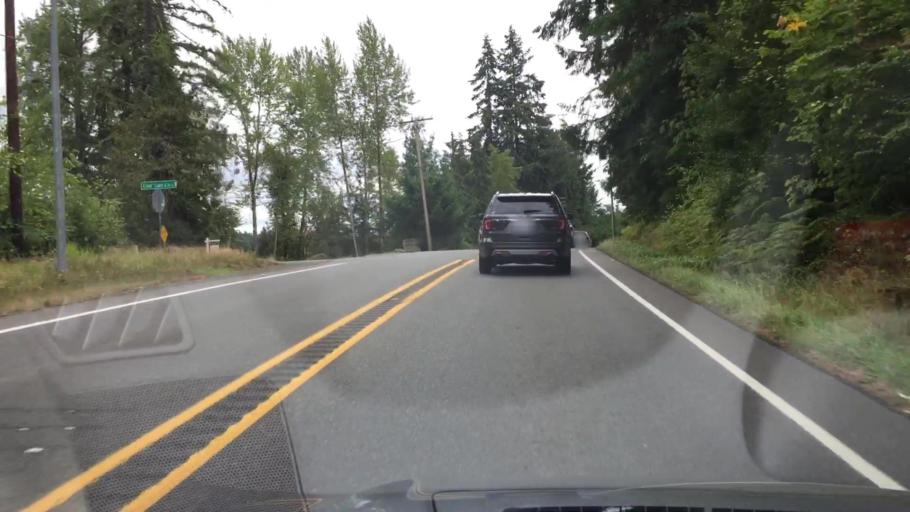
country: US
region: Washington
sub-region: Pierce County
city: Eatonville
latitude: 46.9330
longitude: -122.2824
